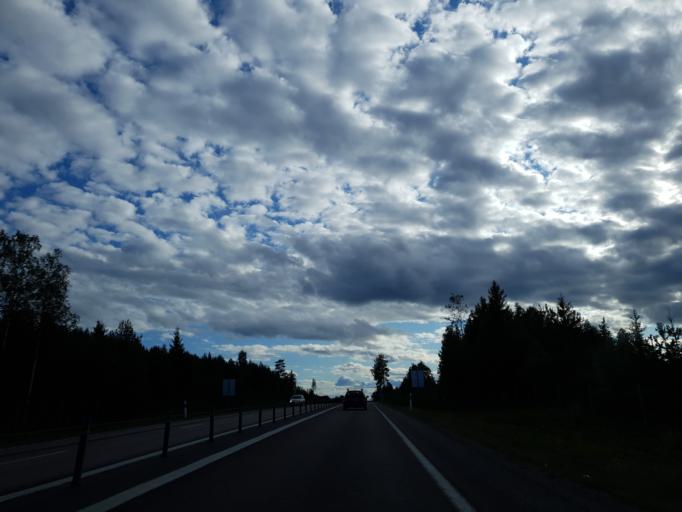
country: SE
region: Vaesternorrland
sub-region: Haernoesands Kommun
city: Haernoesand
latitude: 62.6032
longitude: 17.8160
